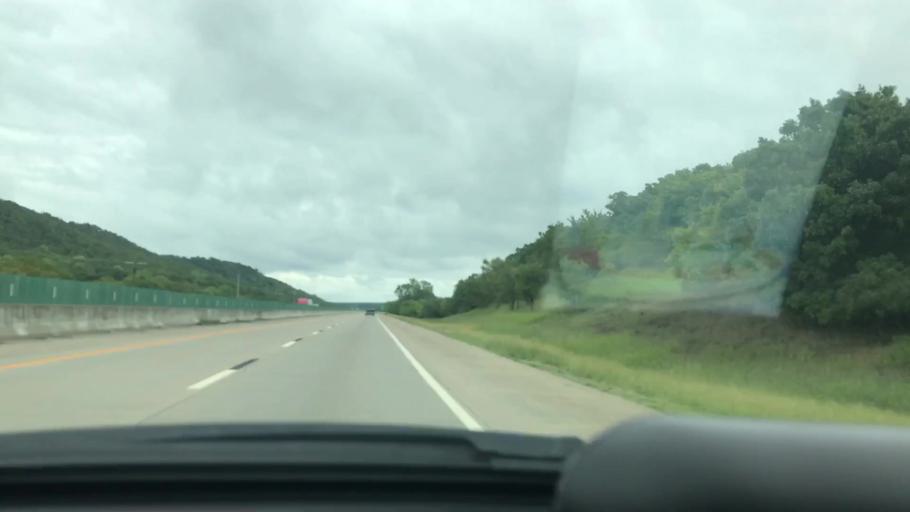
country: US
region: Oklahoma
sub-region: Pittsburg County
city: Krebs
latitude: 35.1124
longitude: -95.6906
